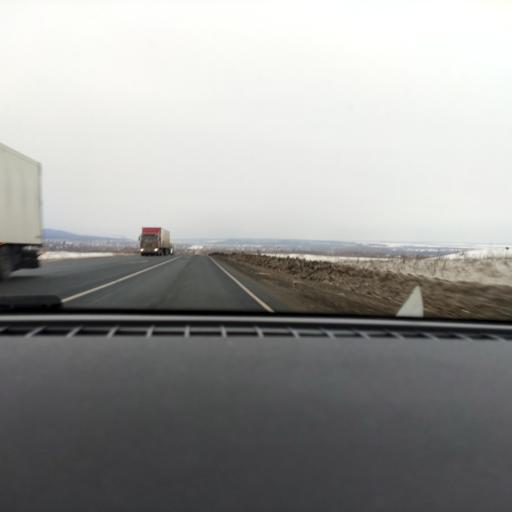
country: RU
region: Samara
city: Novosemeykino
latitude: 53.4069
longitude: 50.3651
